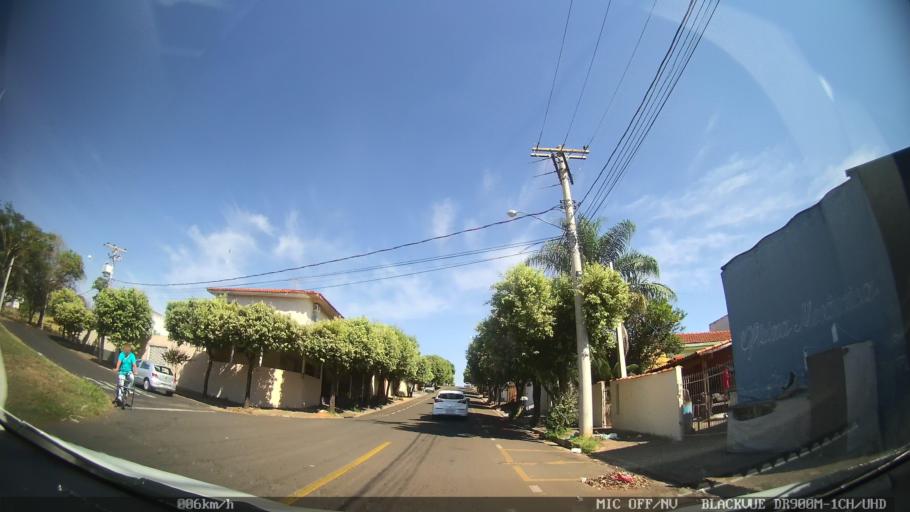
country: BR
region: Sao Paulo
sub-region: Sao Jose Do Rio Preto
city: Sao Jose do Rio Preto
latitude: -20.7740
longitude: -49.4012
